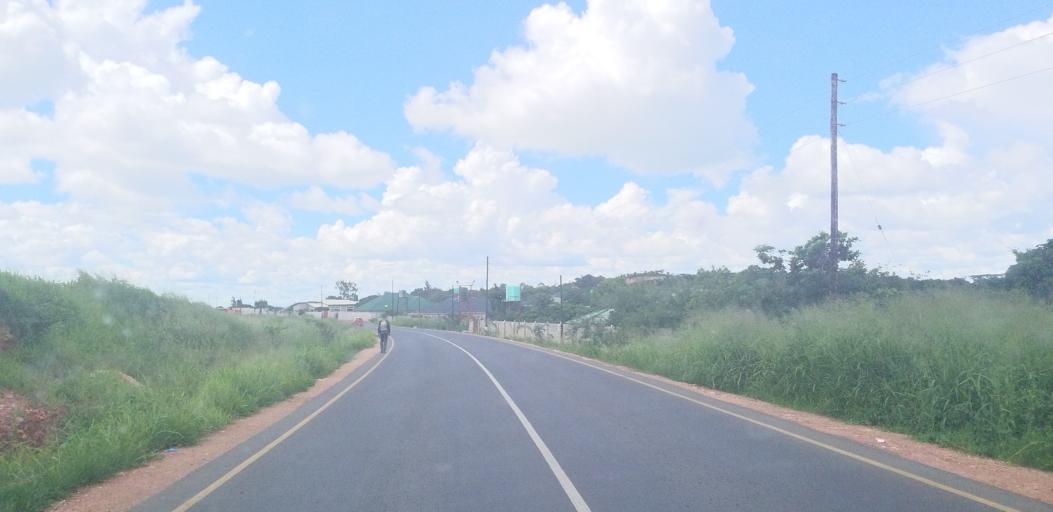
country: ZM
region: Lusaka
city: Lusaka
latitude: -15.3302
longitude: 28.3289
